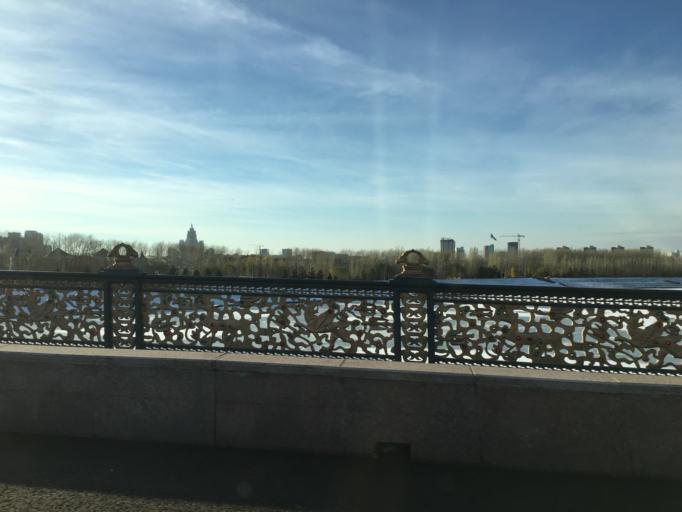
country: KZ
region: Astana Qalasy
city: Astana
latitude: 51.1389
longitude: 71.4441
